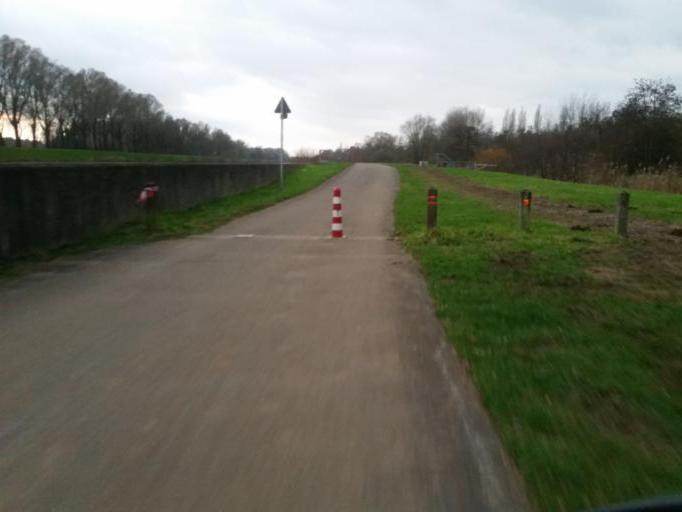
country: BE
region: Flanders
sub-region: Provincie Antwerpen
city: Nijlen
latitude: 51.1749
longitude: 4.6352
